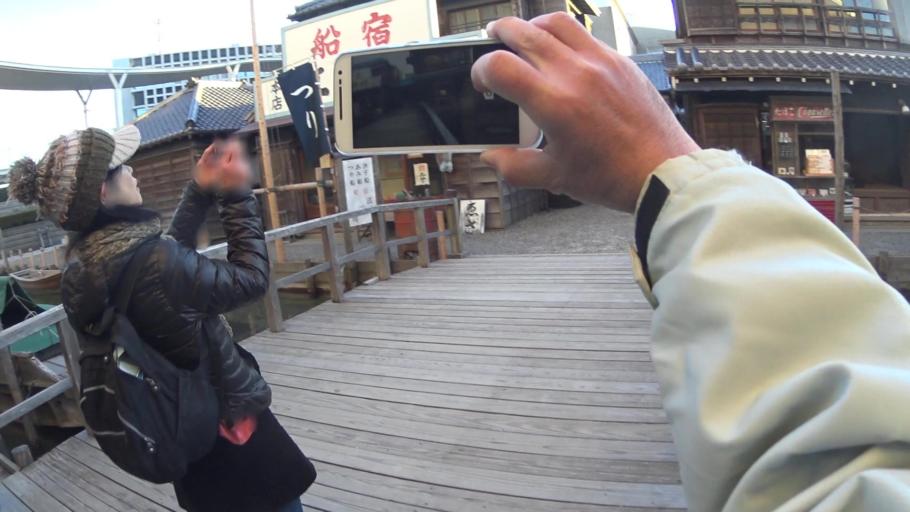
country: JP
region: Tokyo
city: Urayasu
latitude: 35.6567
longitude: 139.9009
